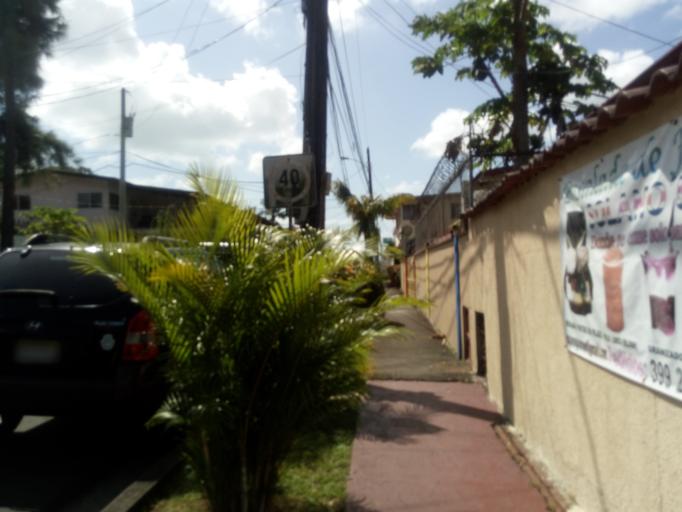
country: PA
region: Panama
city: Panama
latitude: 8.9964
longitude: -79.5380
